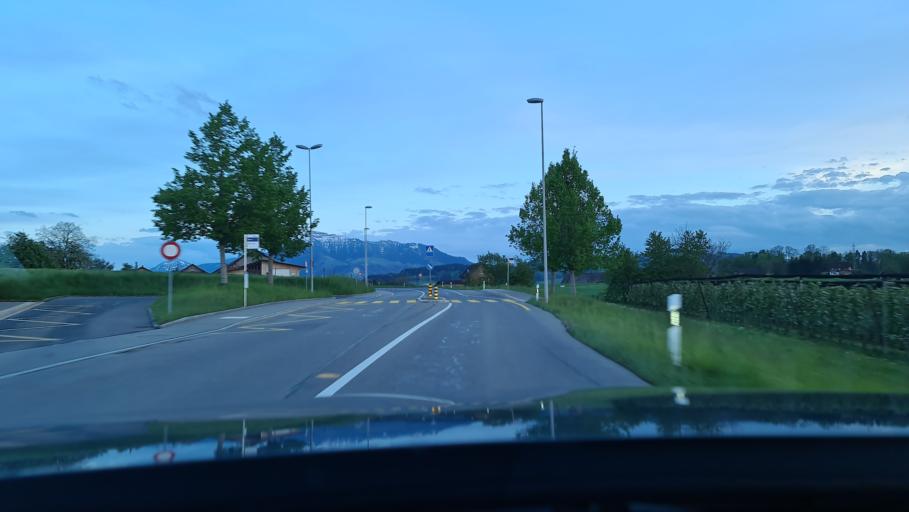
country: CH
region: Zug
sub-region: Zug
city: Hunenberg
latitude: 47.1699
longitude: 8.4279
